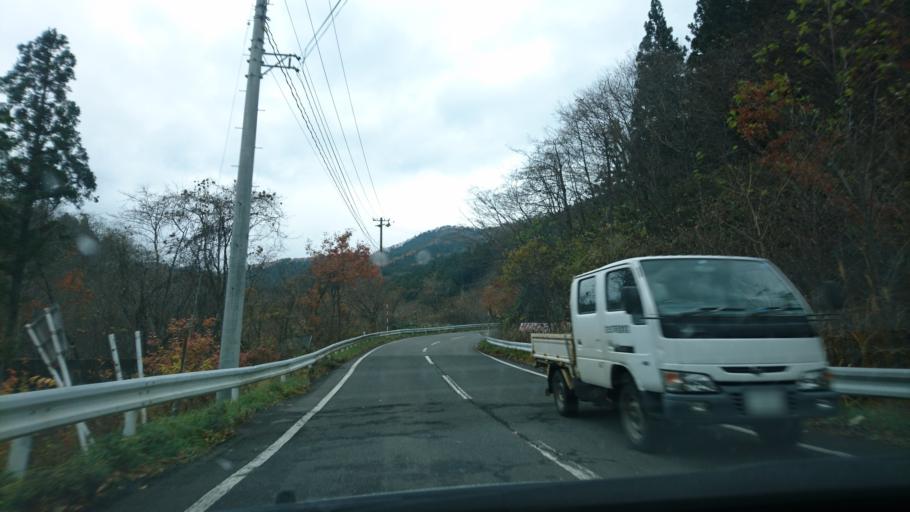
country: JP
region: Iwate
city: Ichinoseki
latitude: 38.9108
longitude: 140.8813
